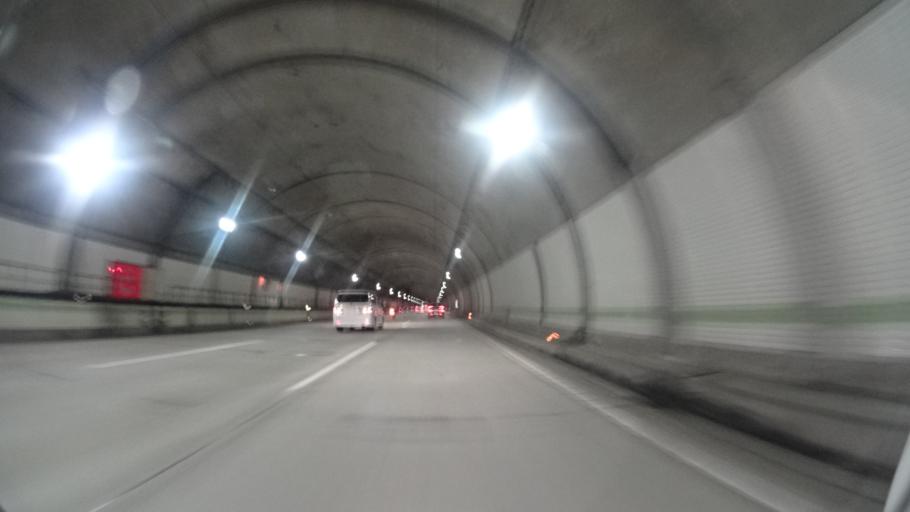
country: JP
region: Hyogo
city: Akashi
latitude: 34.6524
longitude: 135.0611
